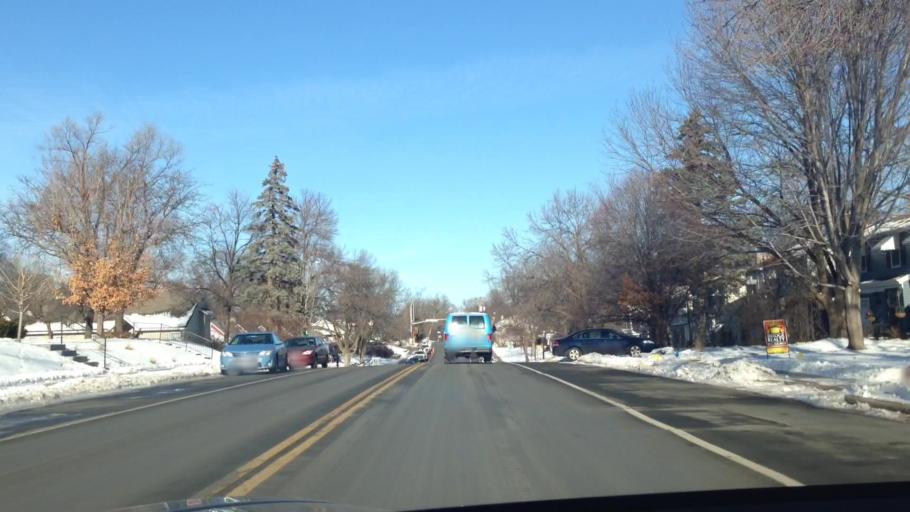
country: US
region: Minnesota
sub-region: Hennepin County
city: Saint Louis Park
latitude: 44.9472
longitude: -93.3605
